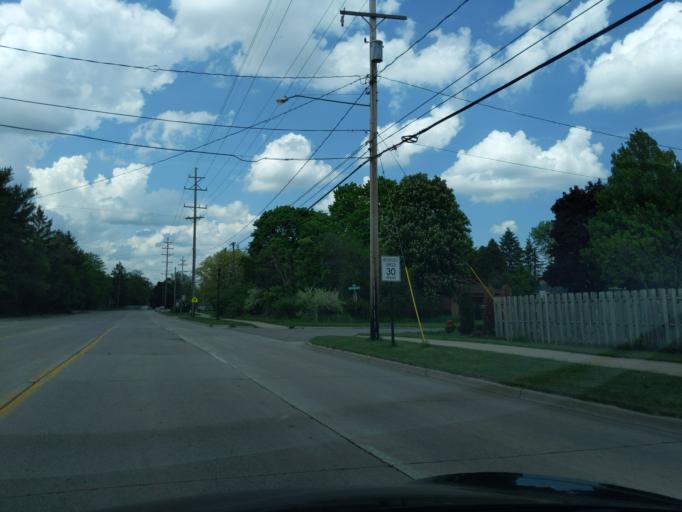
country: US
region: Michigan
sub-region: Ingham County
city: Okemos
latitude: 42.7077
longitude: -84.4324
